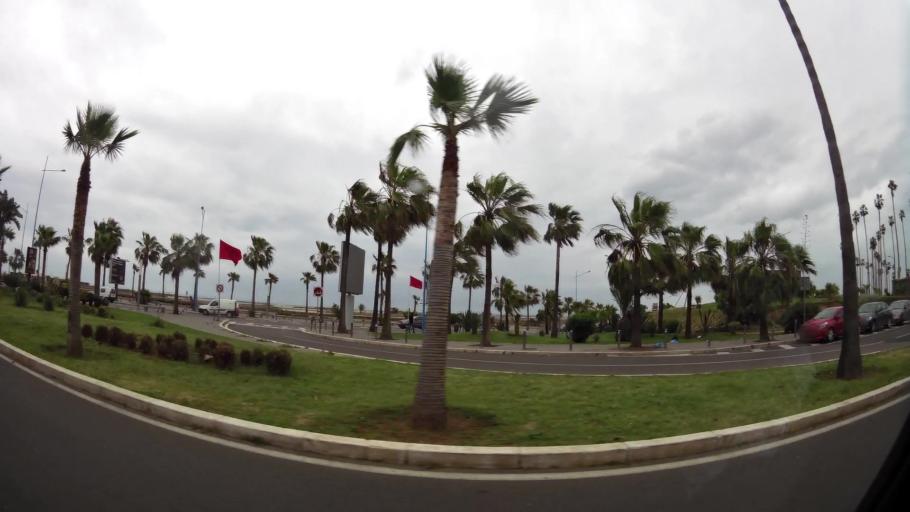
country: MA
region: Grand Casablanca
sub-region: Casablanca
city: Casablanca
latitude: 33.5974
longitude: -7.6636
